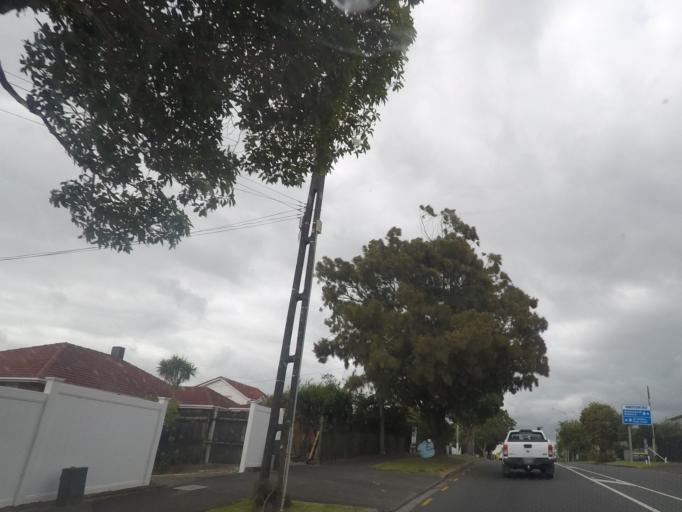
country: NZ
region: Auckland
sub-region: Auckland
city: Tamaki
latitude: -36.8666
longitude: 174.8451
